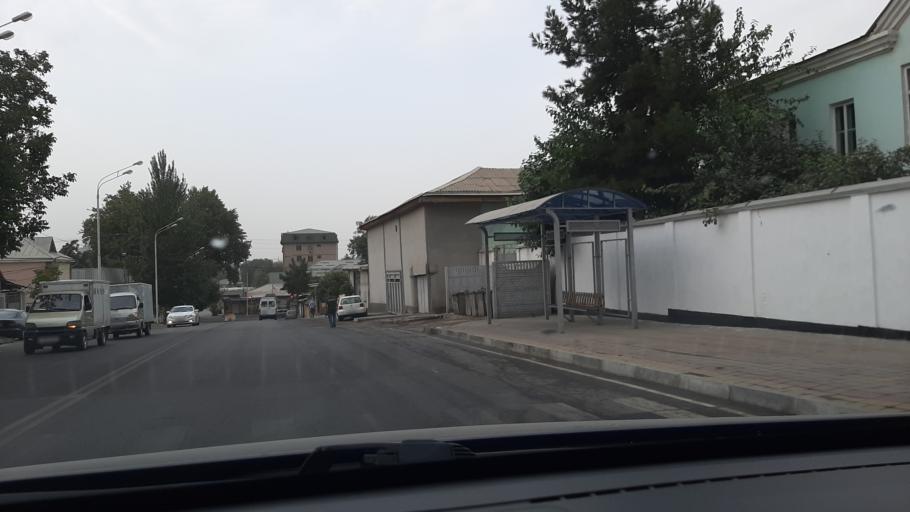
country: TJ
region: Dushanbe
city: Dushanbe
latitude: 38.6098
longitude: 68.7827
